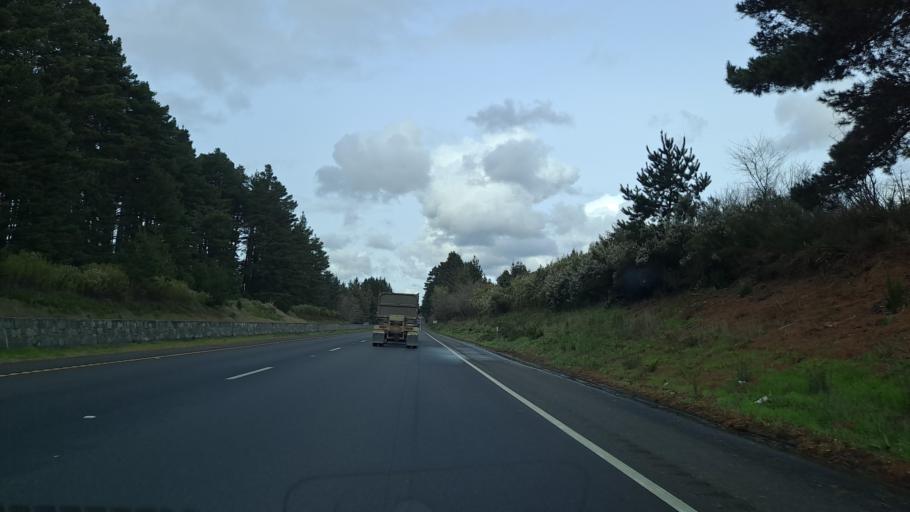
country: US
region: California
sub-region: Humboldt County
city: Fortuna
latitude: 40.6298
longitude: -124.2152
